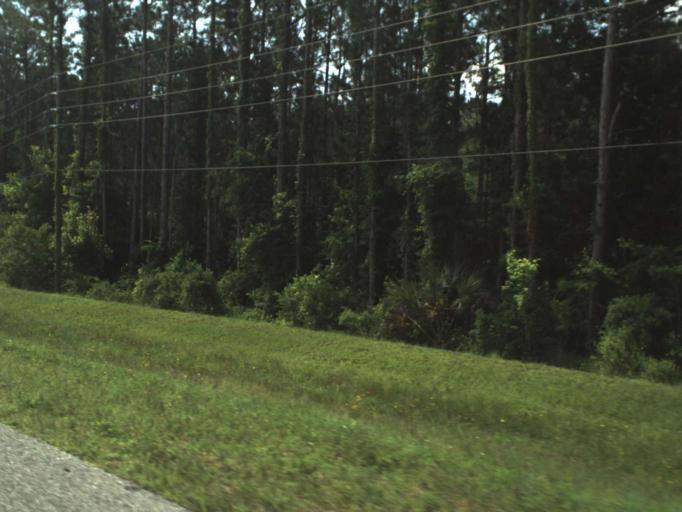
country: US
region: Florida
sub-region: Volusia County
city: Samsula-Spruce Creek
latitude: 29.0232
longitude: -81.1178
